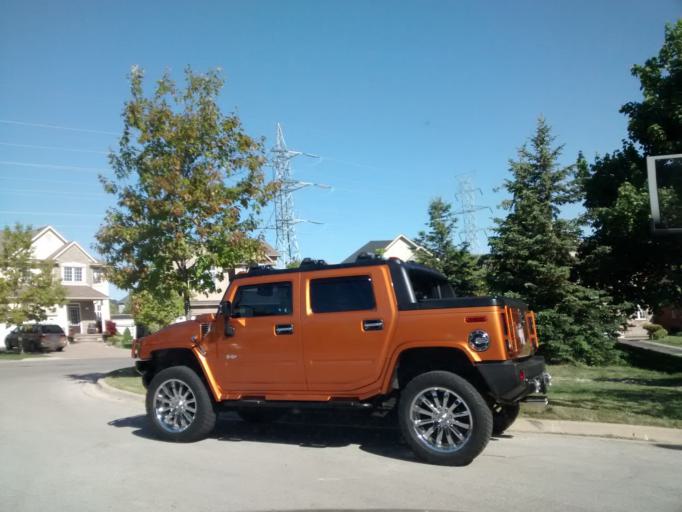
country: CA
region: Ontario
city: Burlington
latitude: 43.3787
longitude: -79.8178
